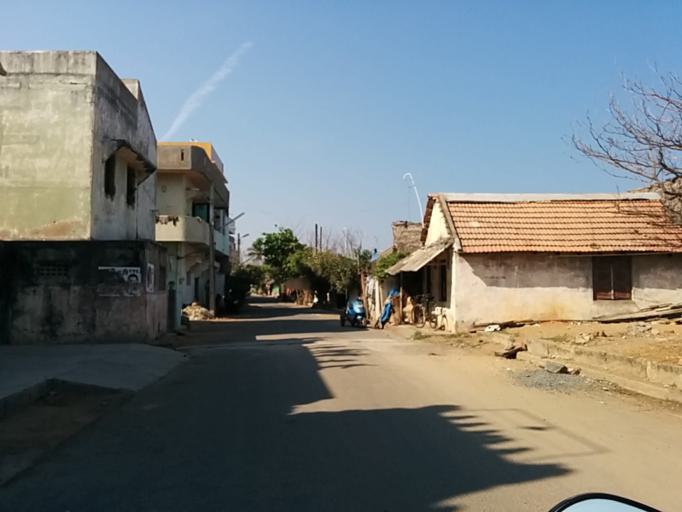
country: IN
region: Pondicherry
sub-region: Puducherry
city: Puducherry
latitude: 11.9419
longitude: 79.8372
